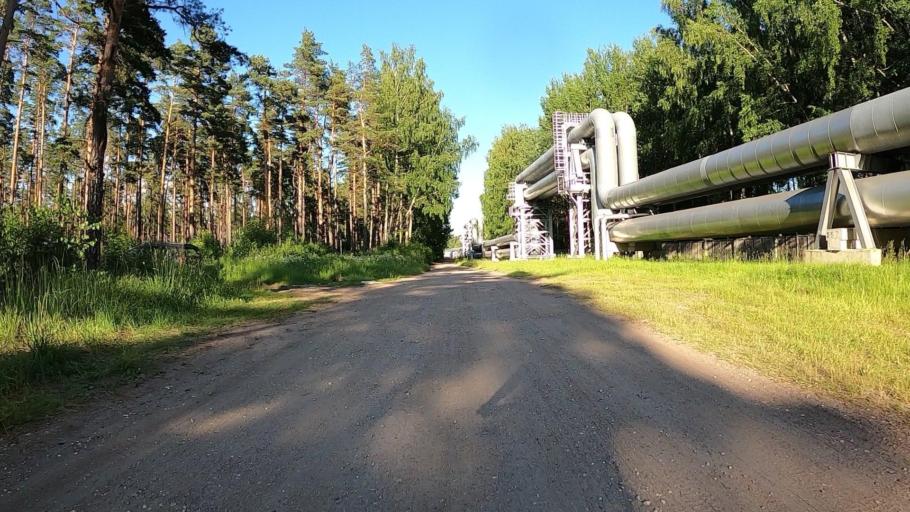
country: LV
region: Stopini
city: Ulbroka
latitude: 56.9227
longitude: 24.2320
